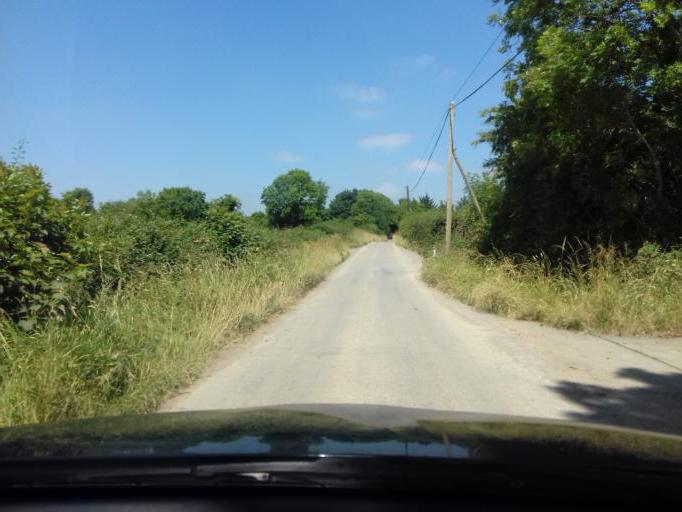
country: IE
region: Leinster
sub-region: Fingal County
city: Swords
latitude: 53.5180
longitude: -6.2358
